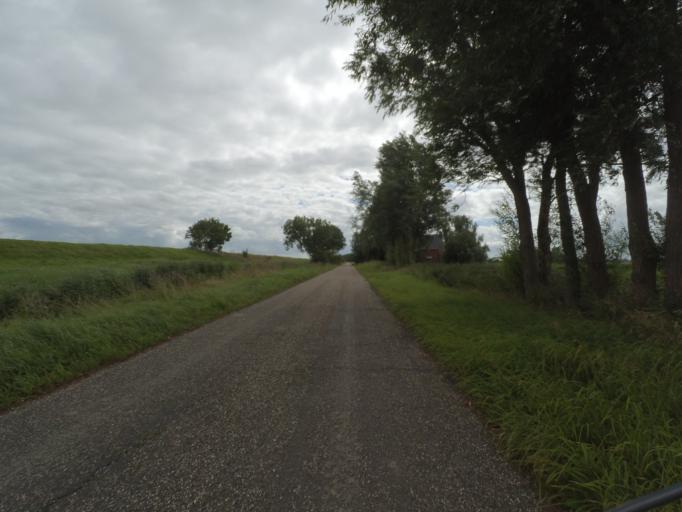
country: NL
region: Friesland
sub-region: Gemeente Dongeradeel
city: Anjum
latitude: 53.3354
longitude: 6.1535
